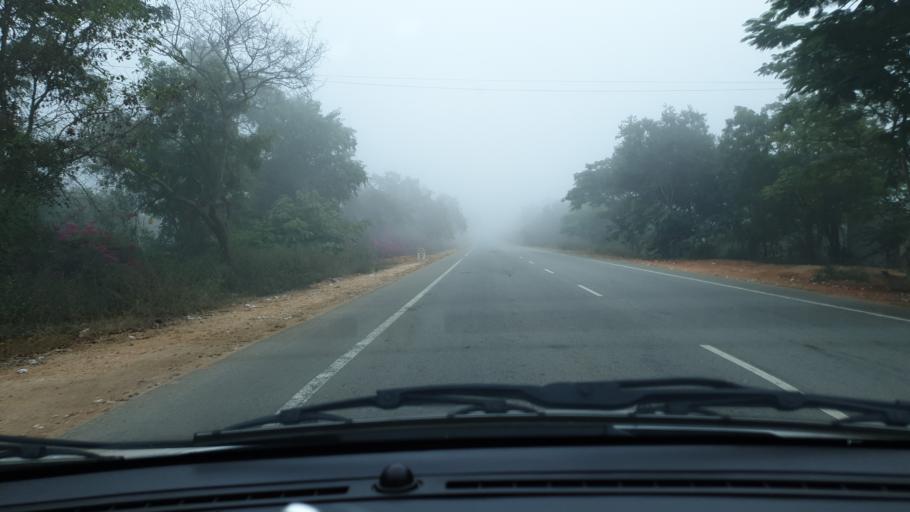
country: IN
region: Telangana
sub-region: Mahbubnagar
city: Nagar Karnul
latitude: 16.6428
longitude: 78.5893
